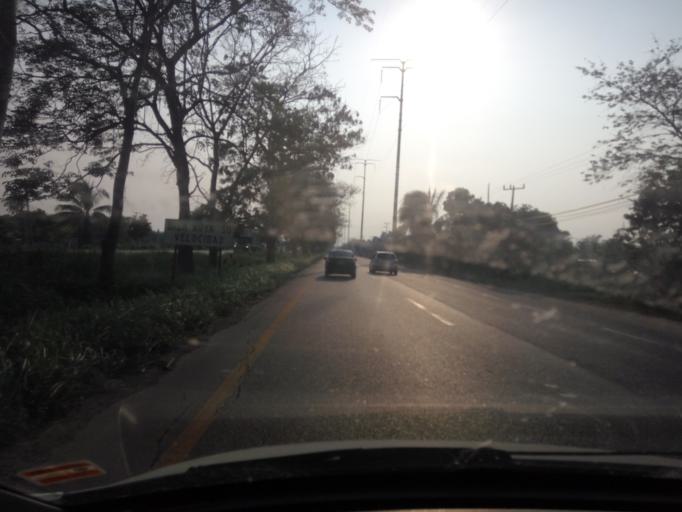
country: MX
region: Tabasco
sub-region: Centro
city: Anacleto Canabal 2da. Seccion
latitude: 17.9794
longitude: -93.0541
